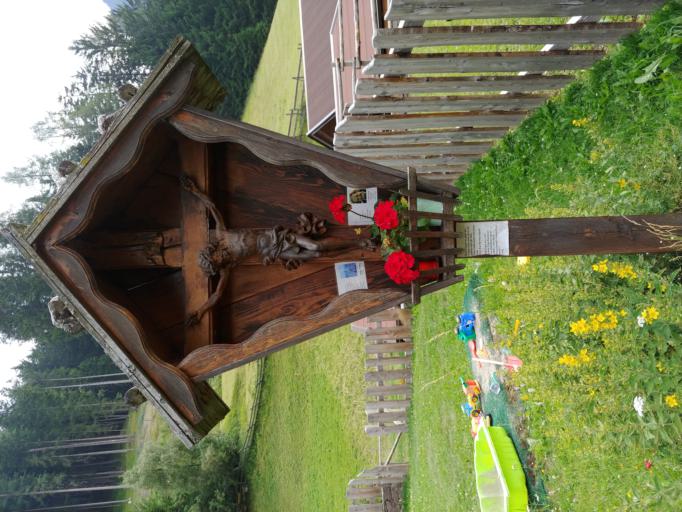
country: IT
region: Trentino-Alto Adige
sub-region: Bolzano
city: Santa Cristina Valgardena
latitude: 46.5584
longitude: 11.7082
